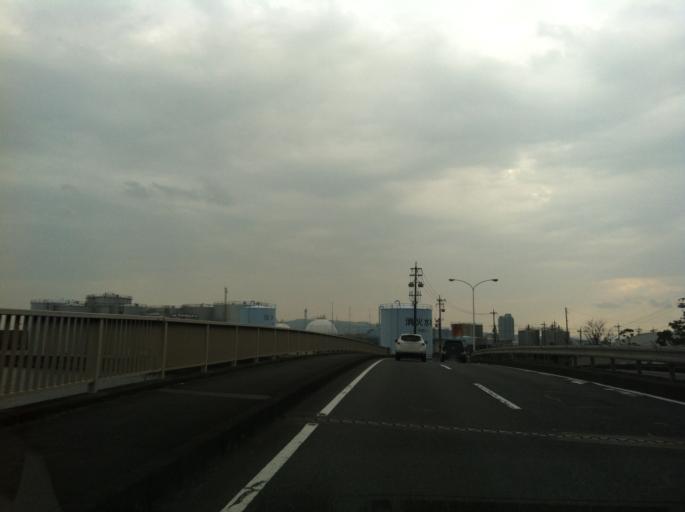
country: JP
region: Shizuoka
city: Shizuoka-shi
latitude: 35.0367
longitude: 138.5004
